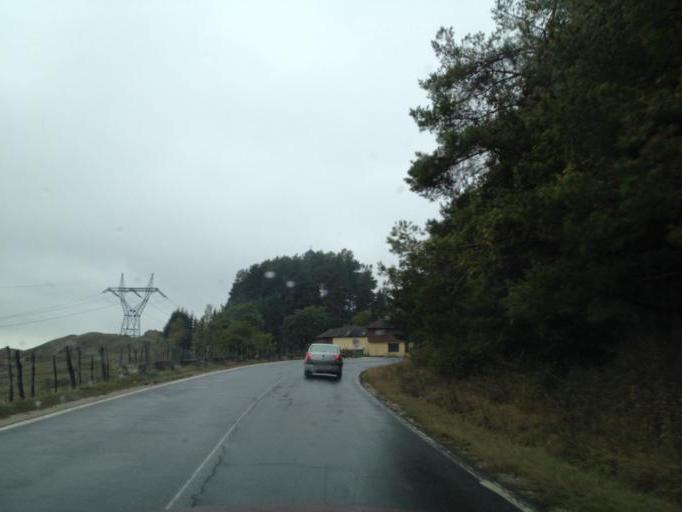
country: RO
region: Arges
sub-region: Comuna Valea Mare-Pravat
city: Valea Mare Pravat
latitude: 45.2941
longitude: 25.1404
